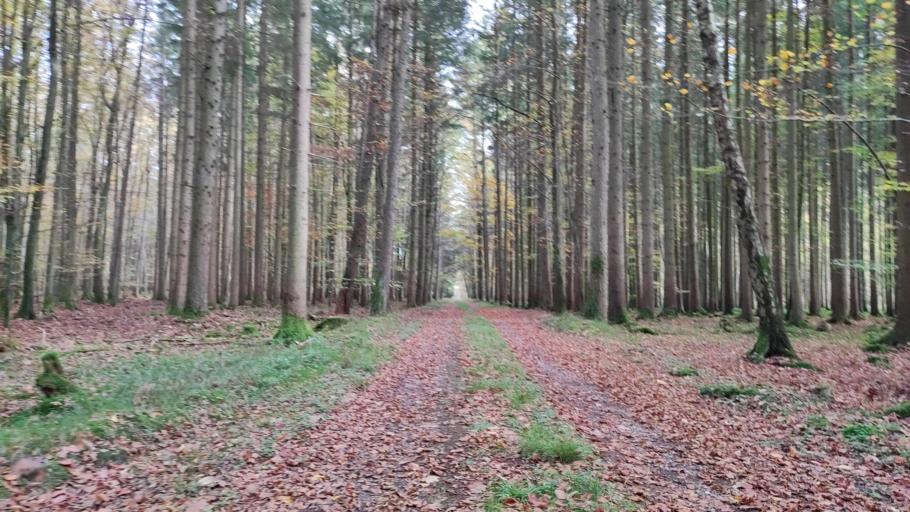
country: DE
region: Bavaria
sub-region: Swabia
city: Burtenbach
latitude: 48.3349
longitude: 10.5002
